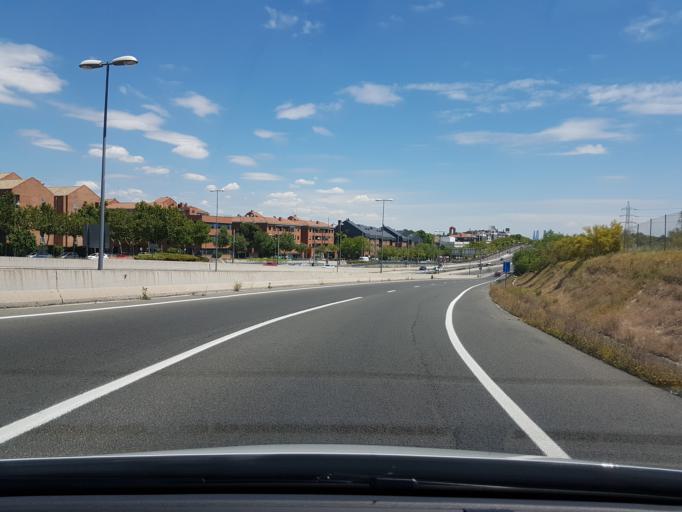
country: ES
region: Madrid
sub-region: Provincia de Madrid
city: Pozuelo de Alarcon
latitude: 40.4291
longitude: -3.8101
